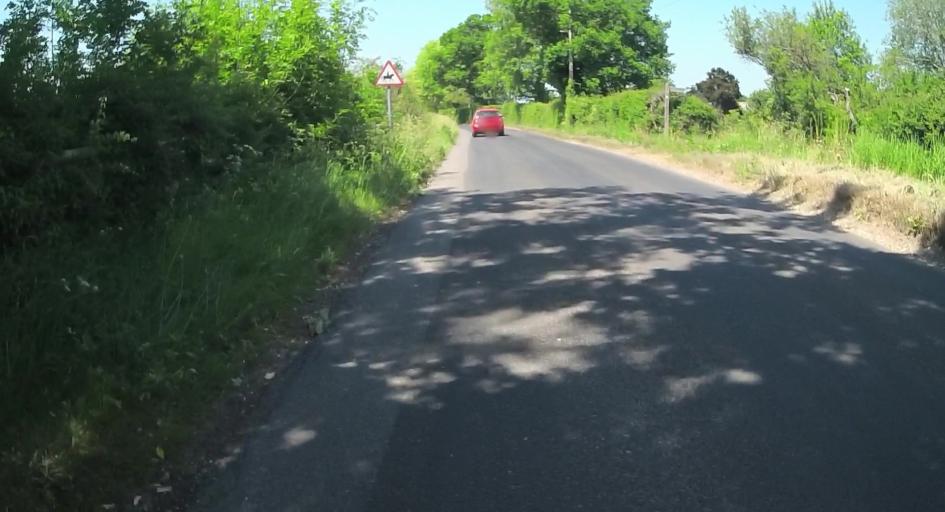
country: GB
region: England
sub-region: Hampshire
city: Tadley
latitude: 51.3207
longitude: -1.1698
